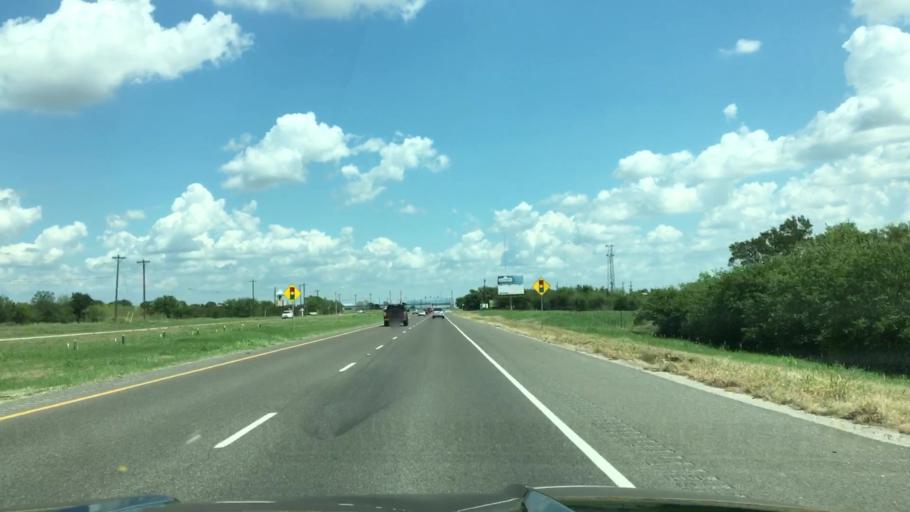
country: US
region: Texas
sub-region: Wise County
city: Rhome
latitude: 33.0365
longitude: -97.4039
